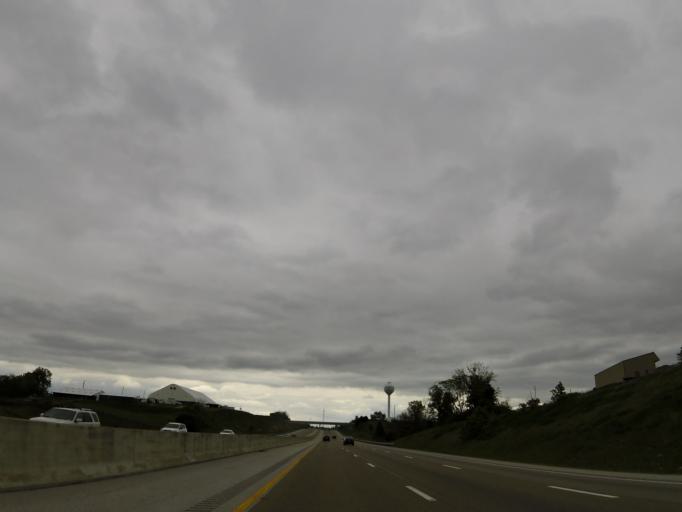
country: US
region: Kentucky
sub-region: Grant County
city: Williamstown
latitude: 38.6036
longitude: -84.5793
